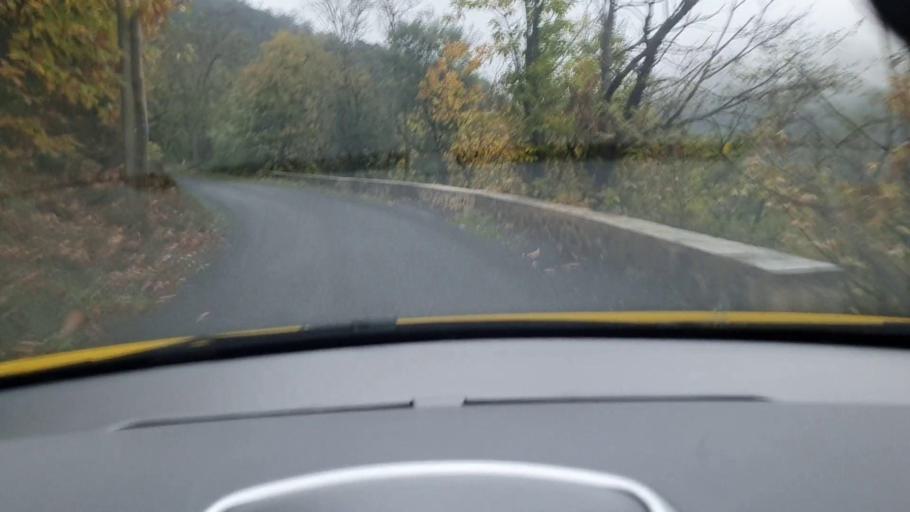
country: FR
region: Languedoc-Roussillon
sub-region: Departement du Gard
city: Sumene
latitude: 44.0352
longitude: 3.7260
